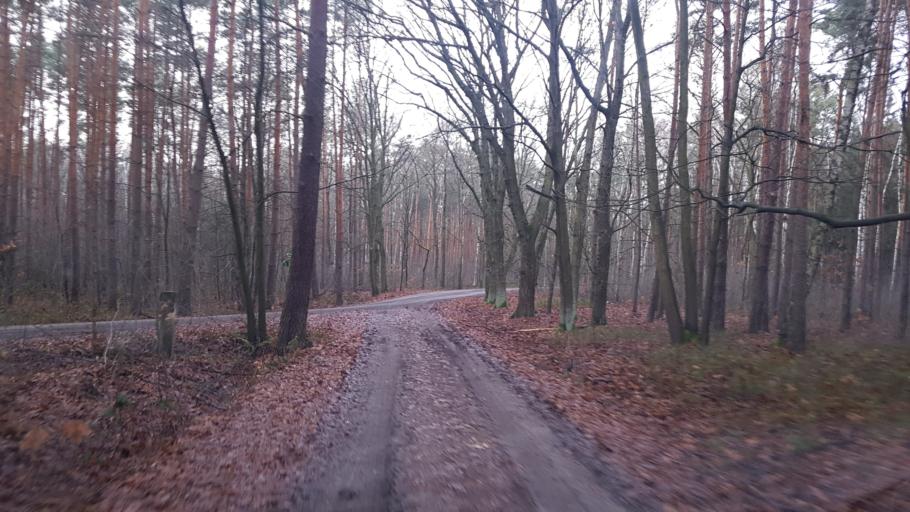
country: DE
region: Brandenburg
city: Ruckersdorf
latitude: 51.5825
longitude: 13.6044
